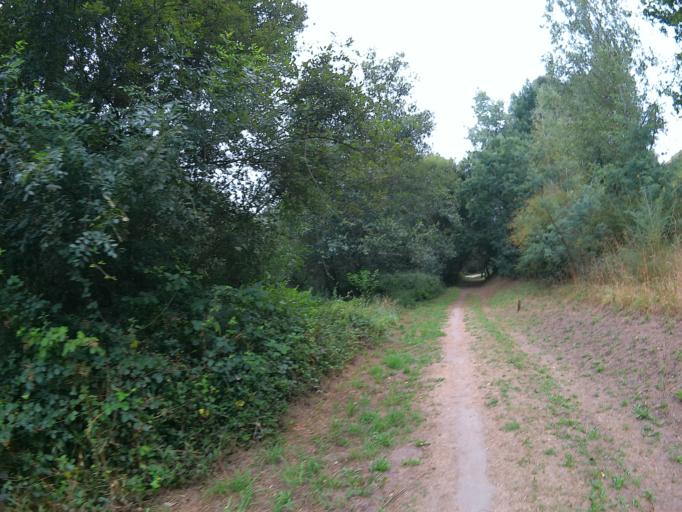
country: PT
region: Viana do Castelo
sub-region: Ponte da Barca
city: Ponte da Barca
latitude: 41.7999
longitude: -8.4745
